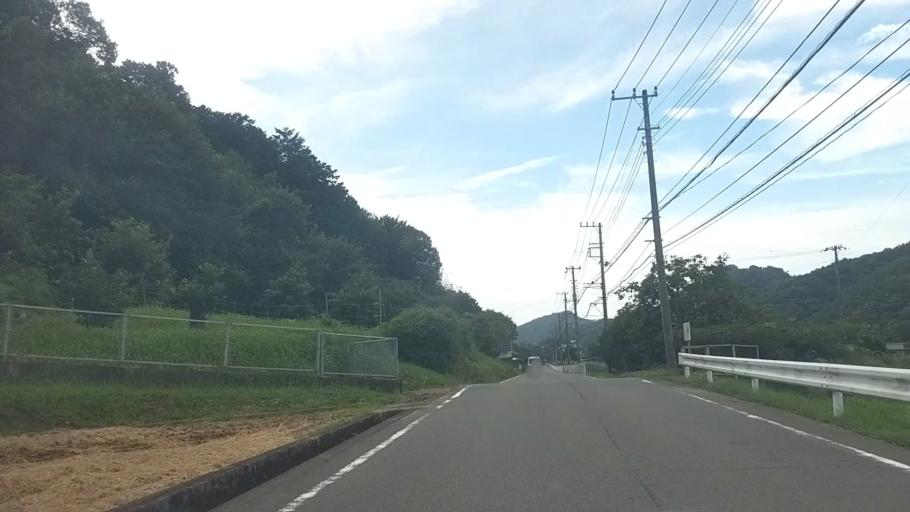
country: JP
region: Shizuoka
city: Ito
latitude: 34.9685
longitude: 138.9664
